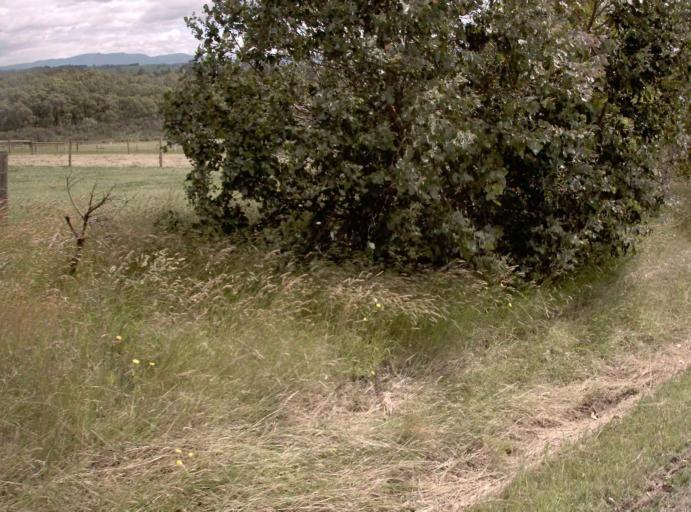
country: AU
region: Victoria
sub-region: Latrobe
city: Moe
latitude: -38.1092
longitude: 146.1568
